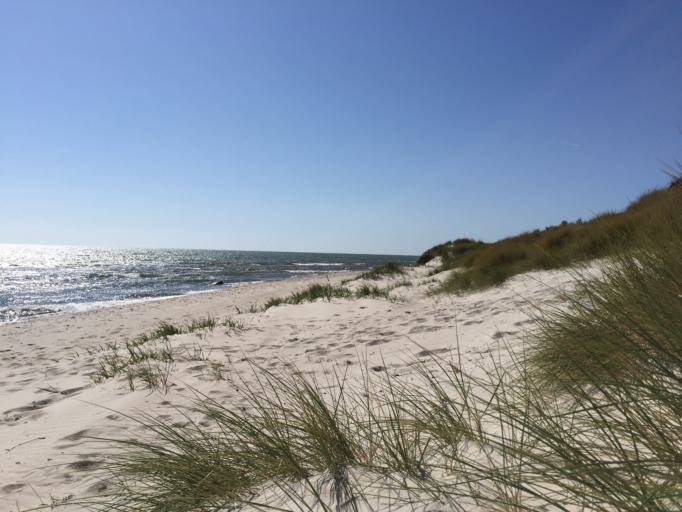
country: DK
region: Capital Region
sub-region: Bornholm Kommune
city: Akirkeby
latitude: 54.9959
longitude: 15.0182
